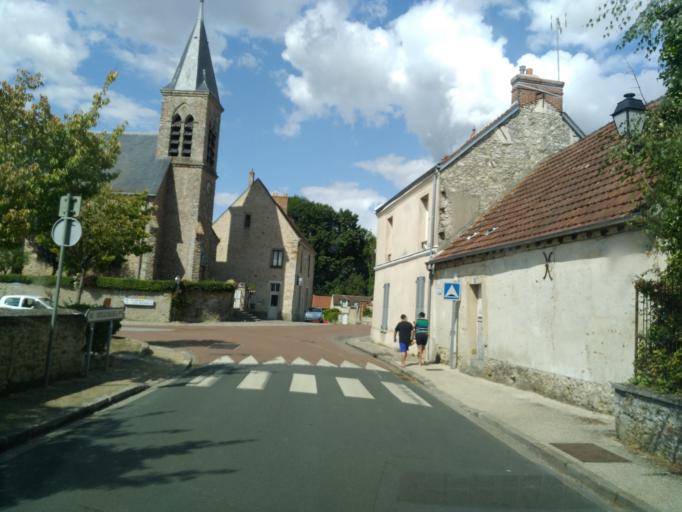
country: FR
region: Ile-de-France
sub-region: Departement des Yvelines
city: Auffargis
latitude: 48.7022
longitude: 1.8850
